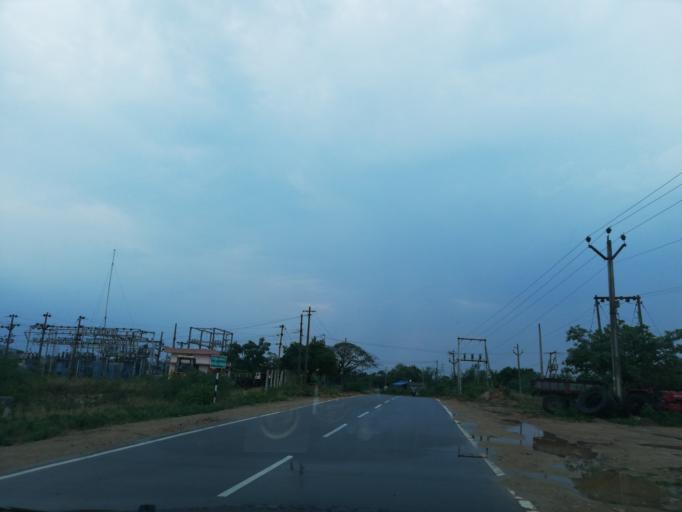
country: IN
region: Andhra Pradesh
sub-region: Guntur
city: Macherla
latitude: 16.6711
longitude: 79.2792
